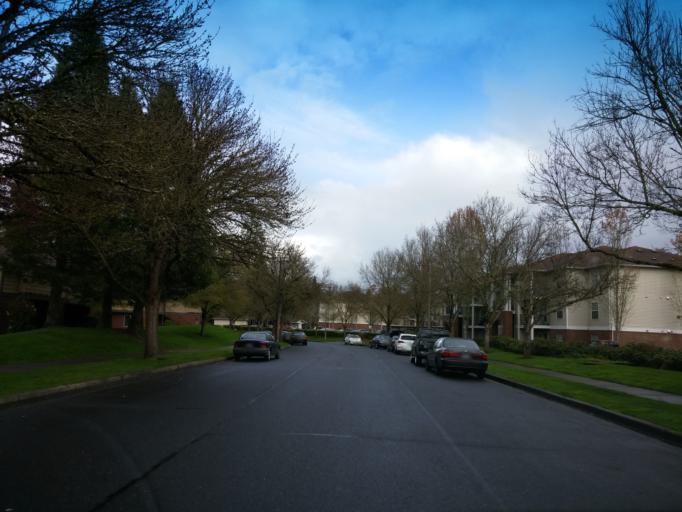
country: US
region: Oregon
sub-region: Washington County
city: Oak Hills
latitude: 45.5137
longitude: -122.8441
